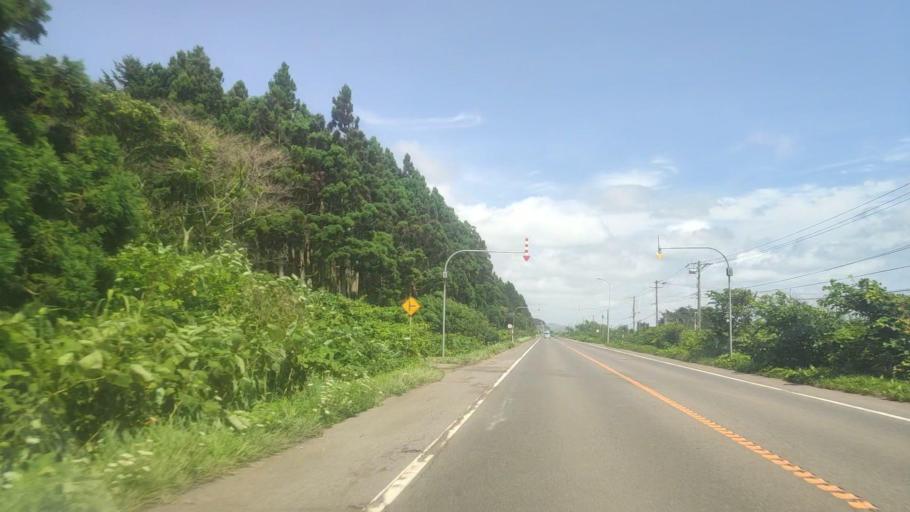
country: JP
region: Hokkaido
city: Niseko Town
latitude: 42.3403
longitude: 140.2806
